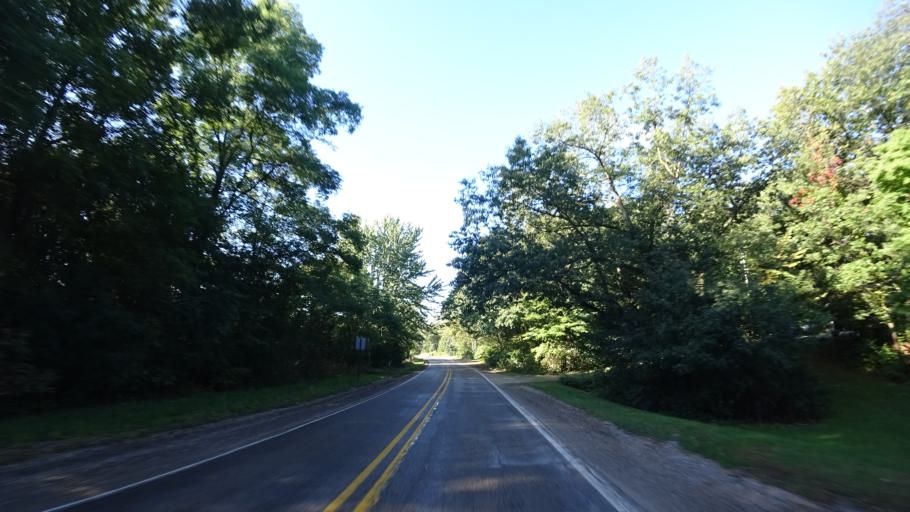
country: US
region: Michigan
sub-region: Kent County
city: Grandville
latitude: 42.9462
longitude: -85.7505
